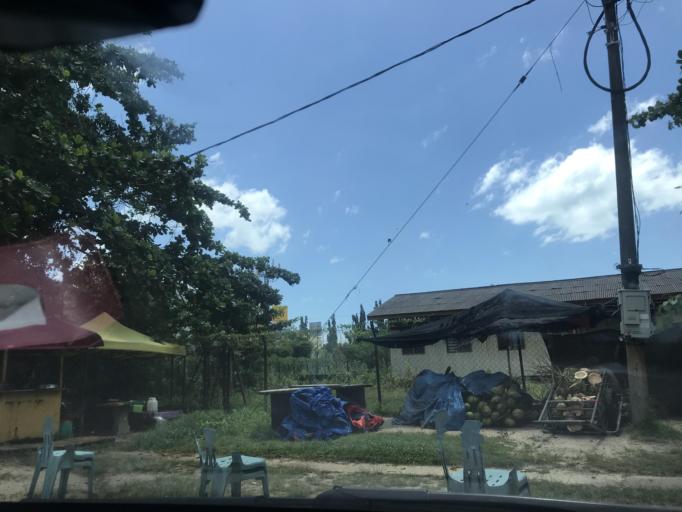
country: TH
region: Narathiwat
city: Tak Bai
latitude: 6.2309
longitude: 102.0923
